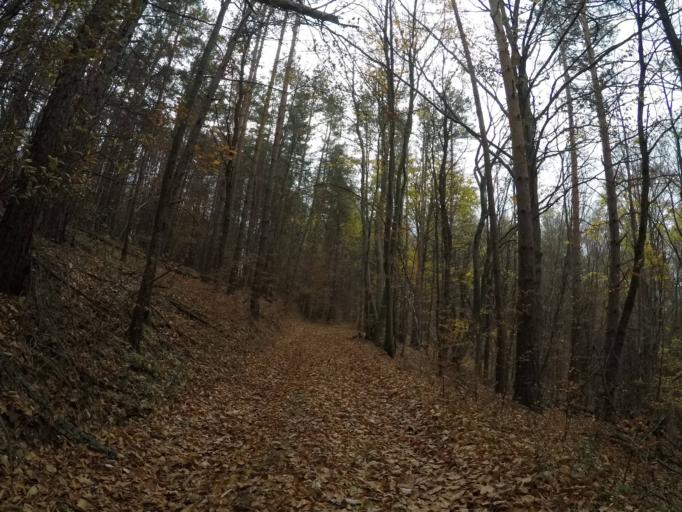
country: SK
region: Presovsky
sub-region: Okres Presov
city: Presov
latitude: 48.9021
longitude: 21.1674
